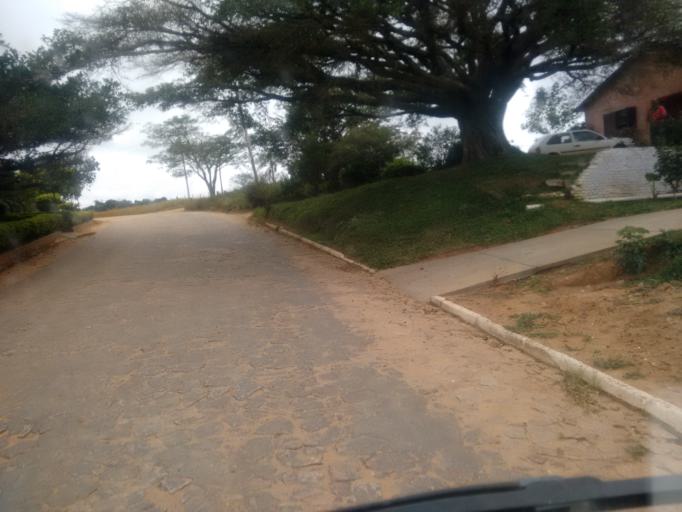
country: BR
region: Rio Grande do Sul
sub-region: Camaqua
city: Camaqua
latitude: -30.7957
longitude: -51.8315
